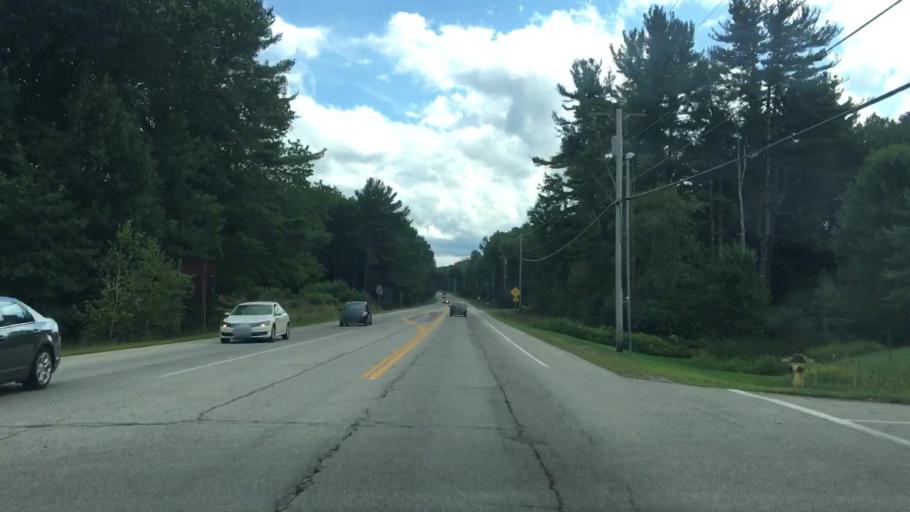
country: US
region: Maine
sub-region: York County
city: South Sanford
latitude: 43.4084
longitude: -70.7424
